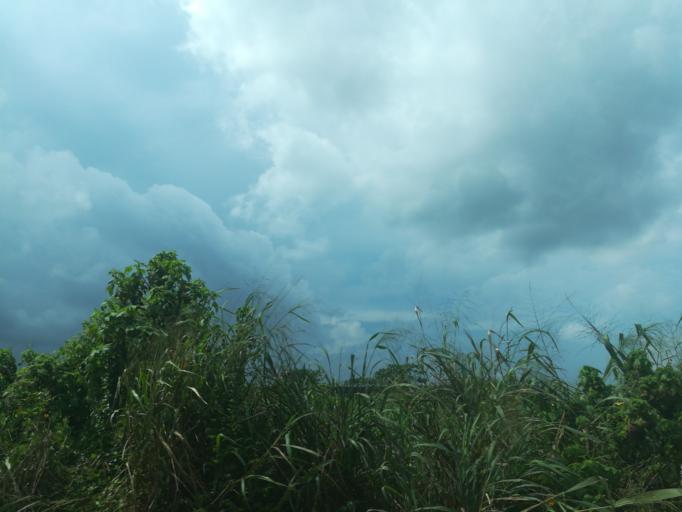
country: NG
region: Lagos
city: Ikorodu
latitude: 6.6466
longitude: 3.5620
